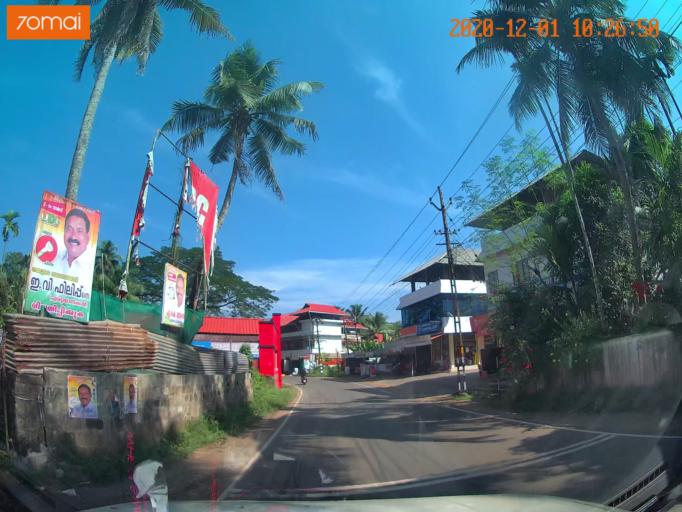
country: IN
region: Kerala
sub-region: Ernakulam
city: Ramamangalam
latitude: 9.9242
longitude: 76.5225
